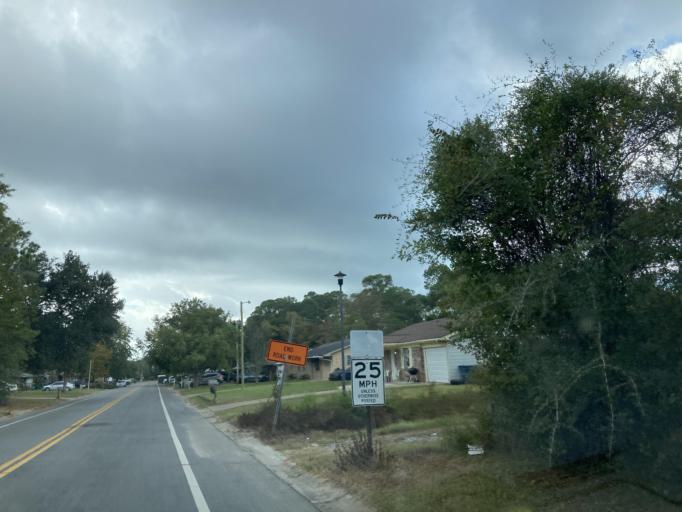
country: US
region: Mississippi
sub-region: Jackson County
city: Gulf Hills
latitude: 30.4386
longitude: -88.8212
